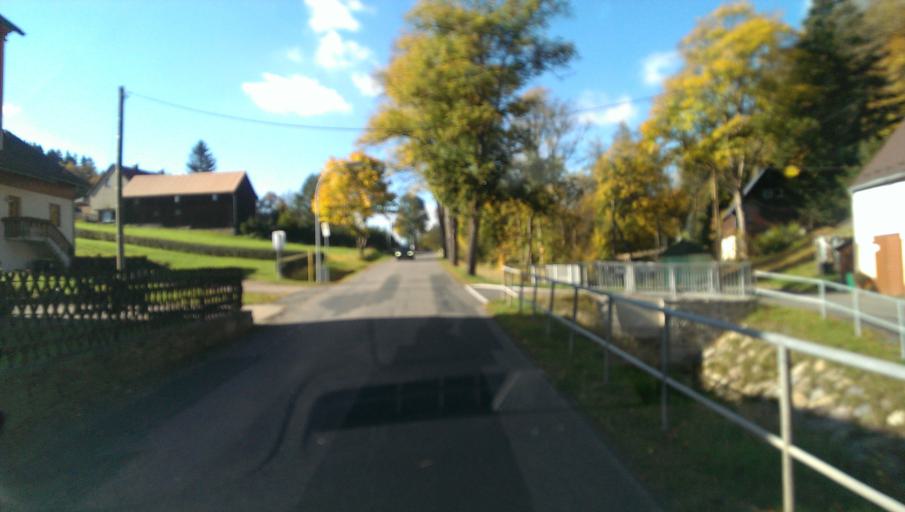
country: DE
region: Saxony
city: Mulda
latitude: 50.8113
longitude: 13.3970
